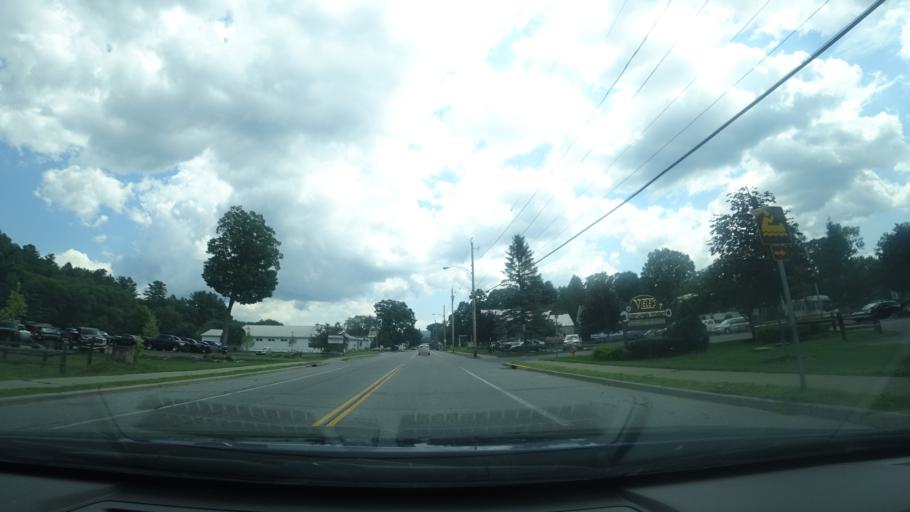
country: US
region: New York
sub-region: Warren County
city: Warrensburg
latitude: 43.5001
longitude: -73.7811
